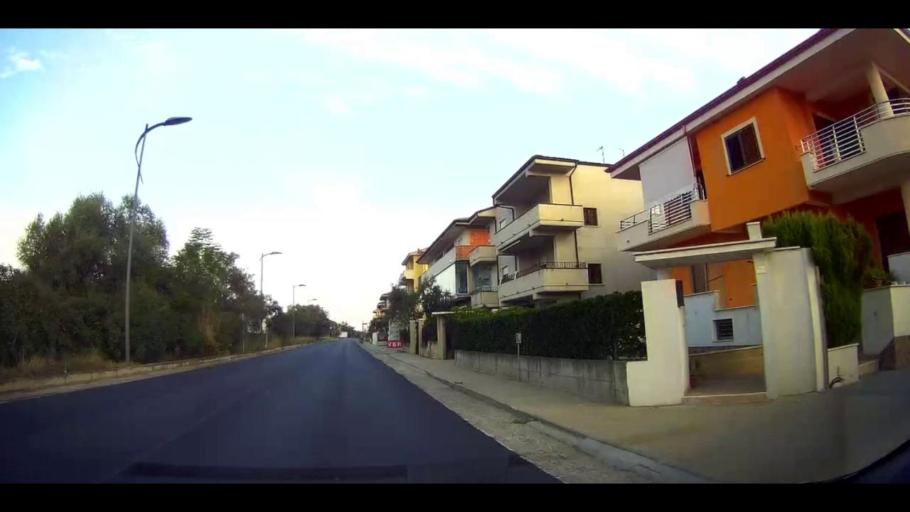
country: IT
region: Calabria
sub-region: Provincia di Crotone
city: Torretta
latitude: 39.4587
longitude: 17.0309
